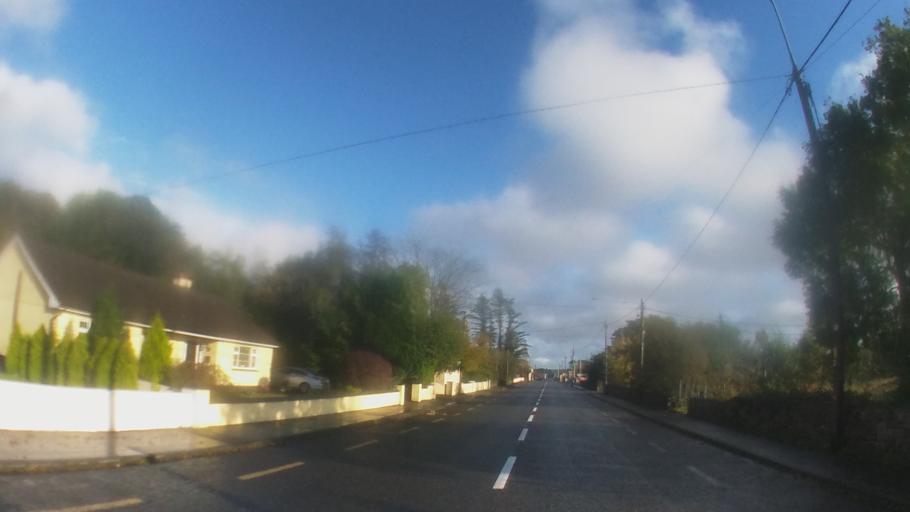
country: IE
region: Connaught
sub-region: Roscommon
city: Ballaghaderreen
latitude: 53.9041
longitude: -8.5847
